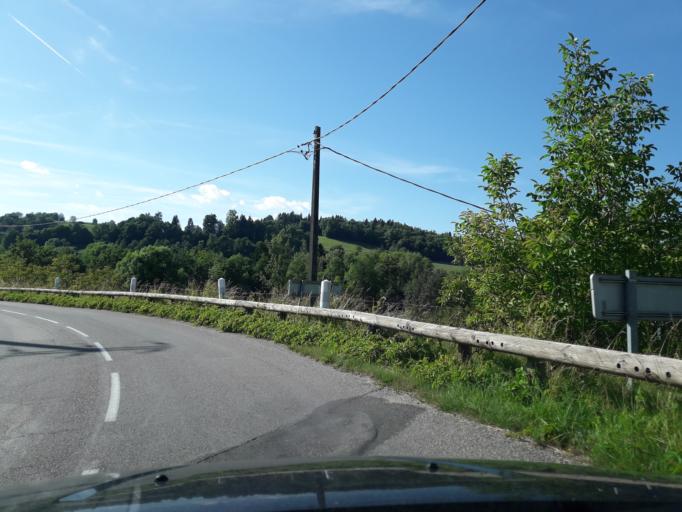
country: FR
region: Rhone-Alpes
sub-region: Departement de la Savoie
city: La Bridoire
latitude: 45.5418
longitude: 5.7721
